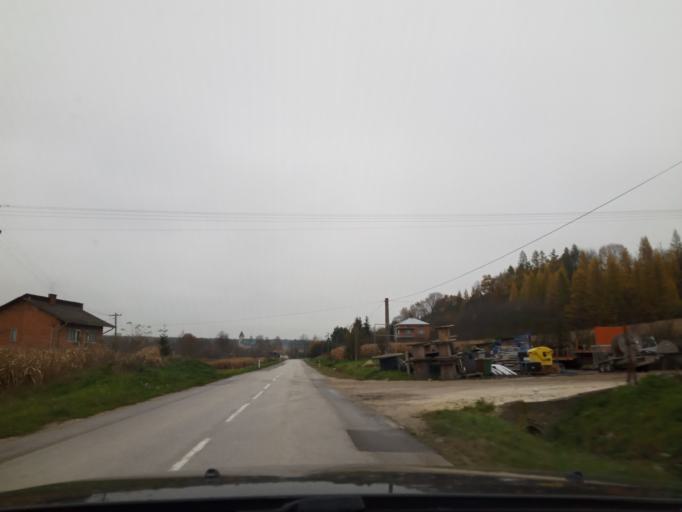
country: PL
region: Swietokrzyskie
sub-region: Powiat pinczowski
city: Dzialoszyce
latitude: 50.4084
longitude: 20.3225
